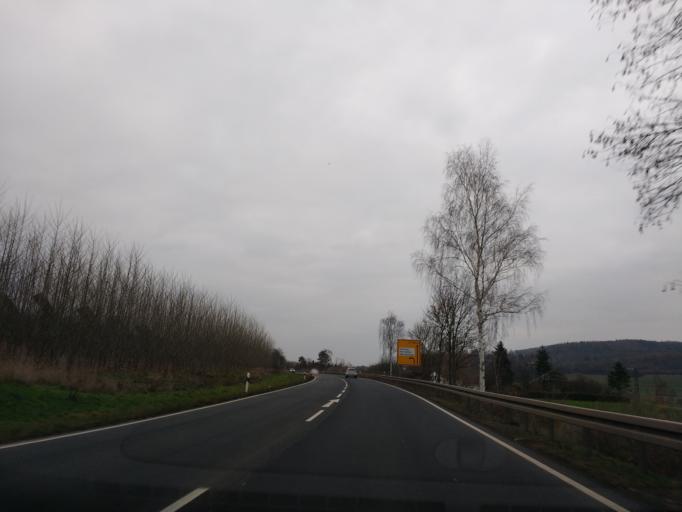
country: DE
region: Hesse
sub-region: Regierungsbezirk Kassel
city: Rotenburg an der Fulda
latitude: 51.0105
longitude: 9.6984
